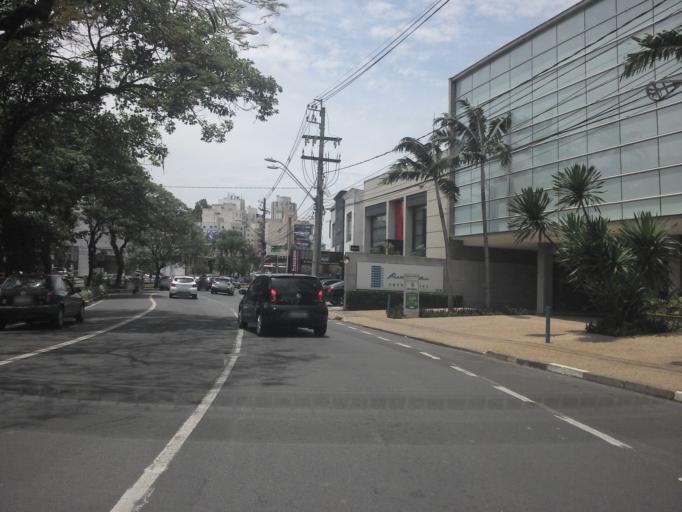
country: BR
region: Sao Paulo
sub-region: Campinas
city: Campinas
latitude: -22.9045
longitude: -47.0475
